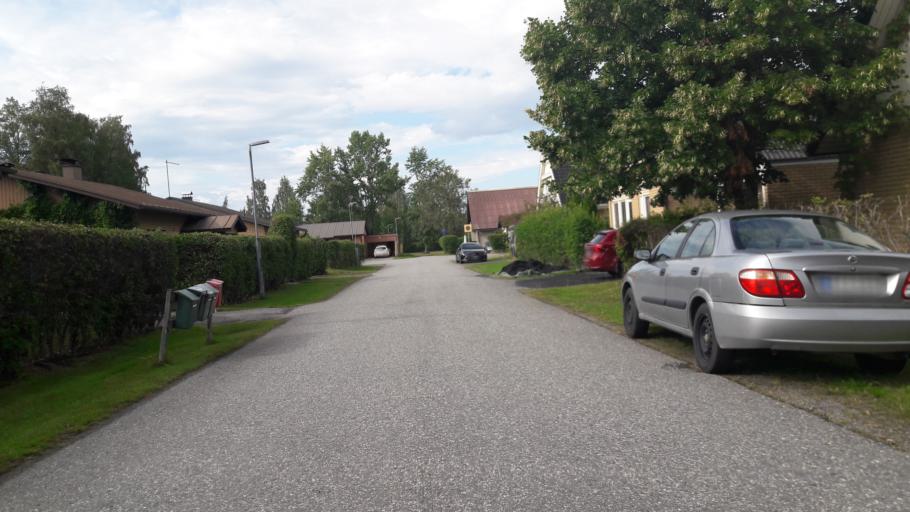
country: FI
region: North Karelia
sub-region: Joensuu
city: Joensuu
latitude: 62.5777
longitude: 29.8129
